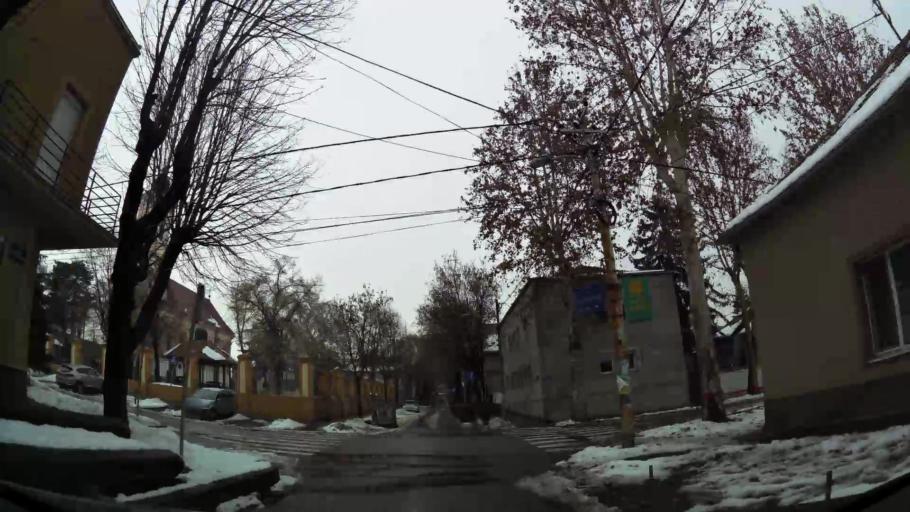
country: RS
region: Central Serbia
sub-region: Belgrade
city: Zemun
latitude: 44.8494
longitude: 20.3961
